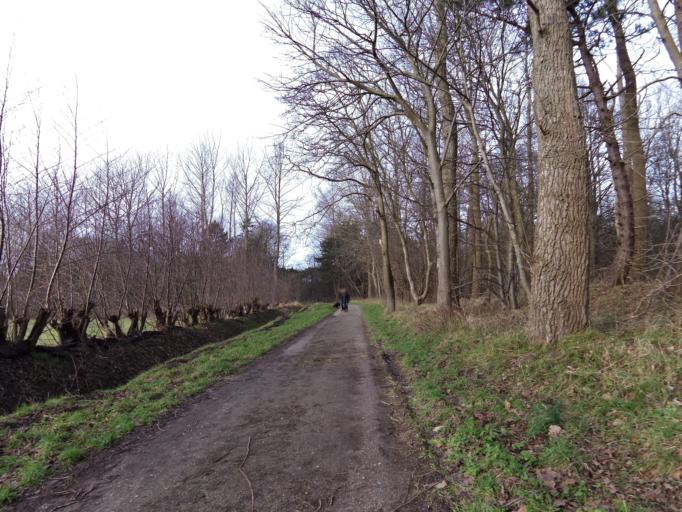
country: NL
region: South Holland
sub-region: Gemeente Brielle
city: Brielle
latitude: 51.9123
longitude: 4.0803
